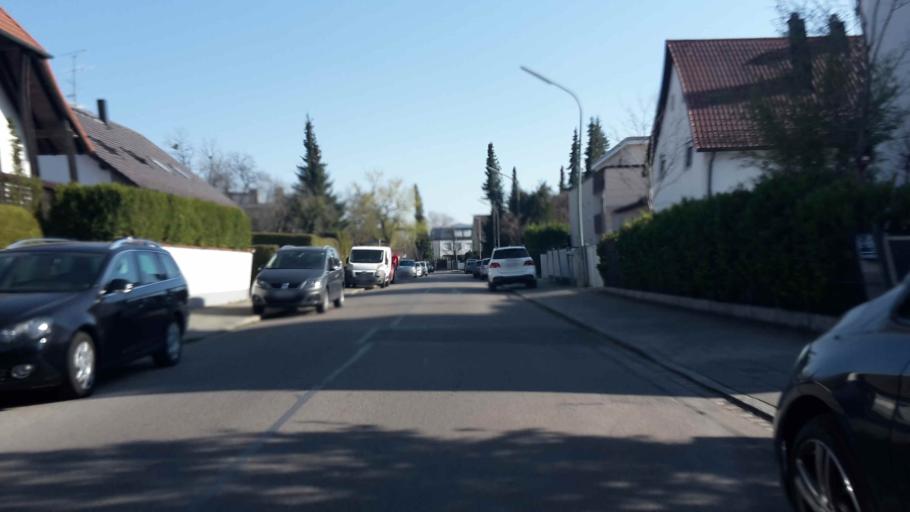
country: DE
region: Bavaria
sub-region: Upper Bavaria
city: Pasing
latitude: 48.1717
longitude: 11.4755
